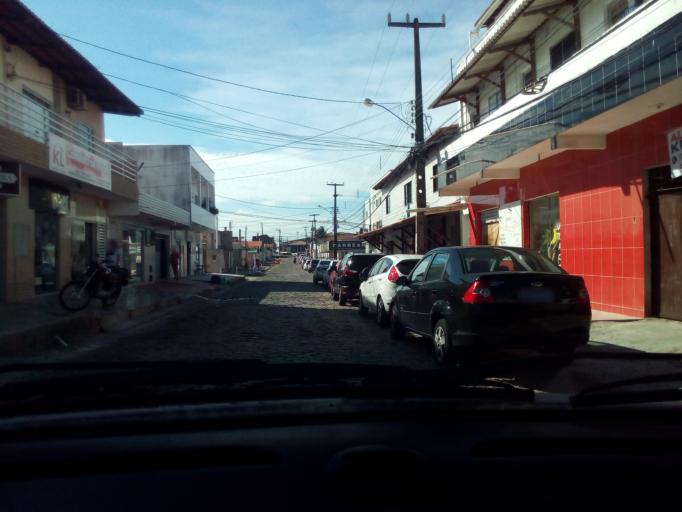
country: BR
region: Rio Grande do Norte
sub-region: Parnamirim
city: Parnamirim
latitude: -5.8876
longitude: -35.2008
